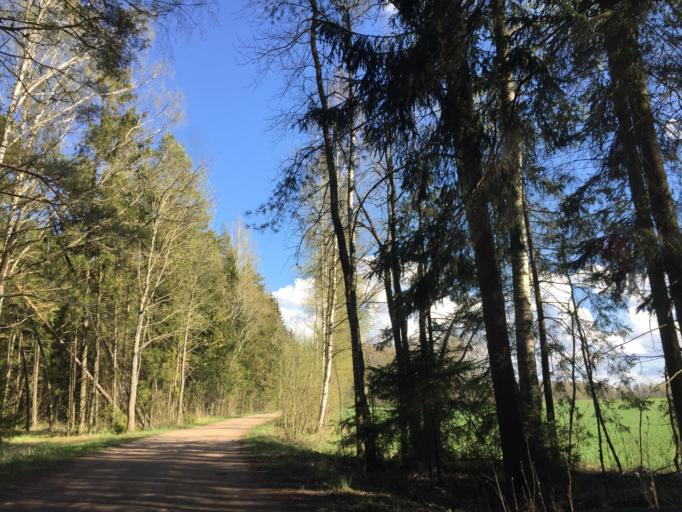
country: LV
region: Beverina
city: Murmuiza
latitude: 57.4988
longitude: 25.5711
